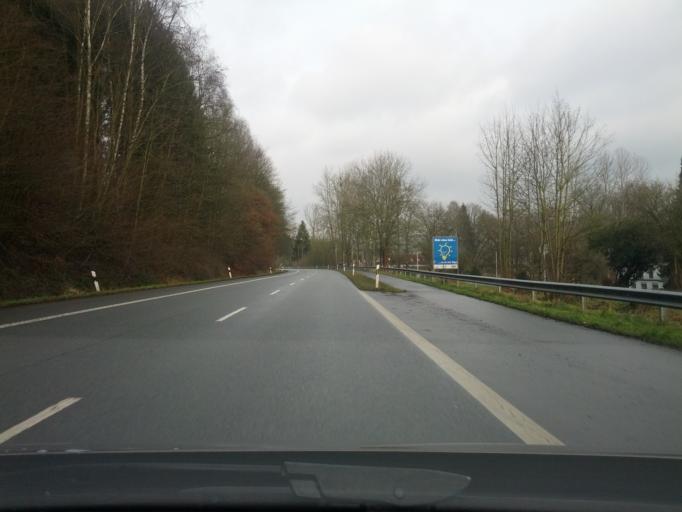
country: DE
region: Lower Saxony
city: Hannoversch Munden
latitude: 51.4273
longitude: 9.6363
